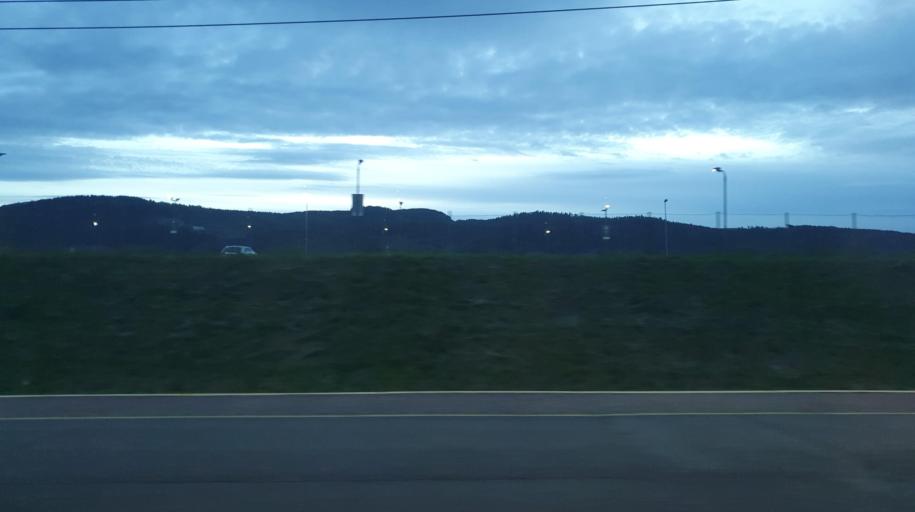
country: NO
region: Vestfold
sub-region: Sande
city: Sande
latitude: 59.5859
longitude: 10.2044
